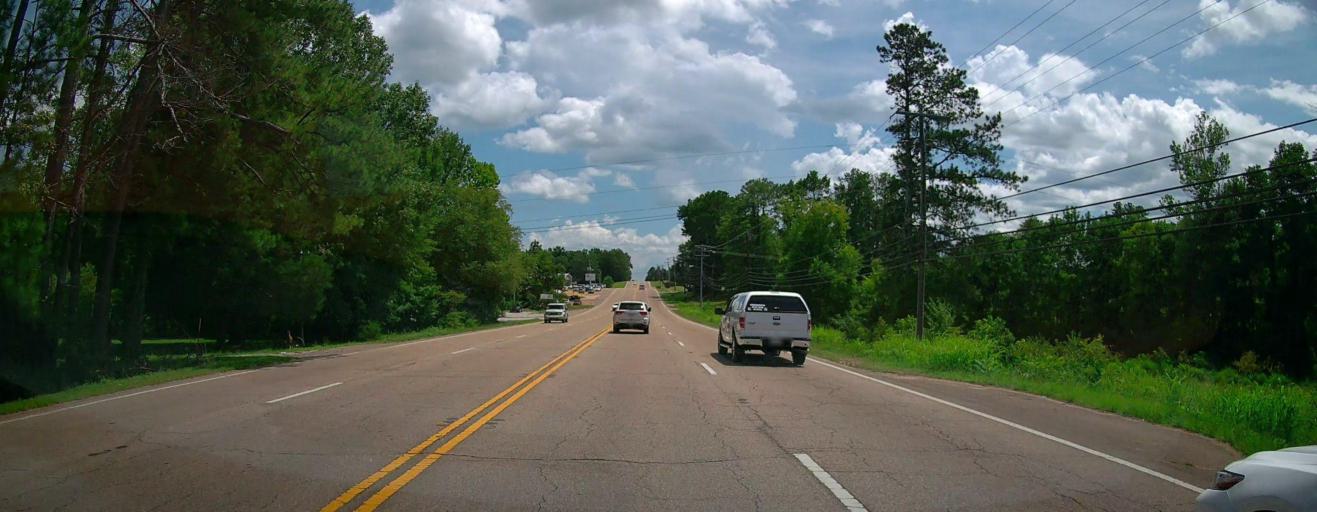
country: US
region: Mississippi
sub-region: Lee County
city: Verona
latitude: 34.1799
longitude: -88.7198
